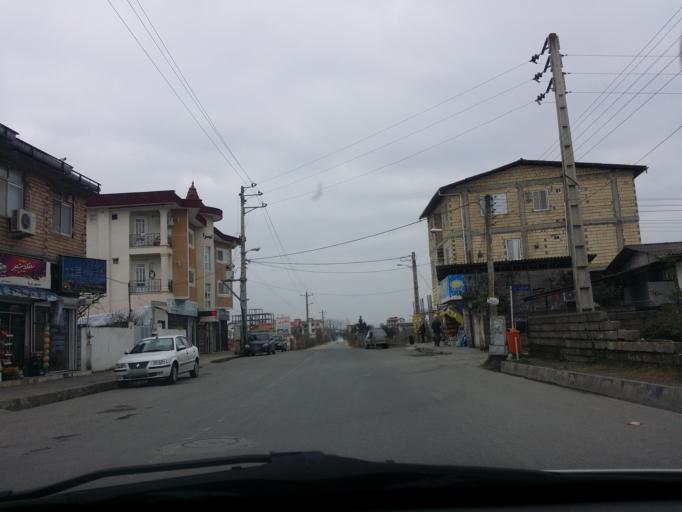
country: IR
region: Mazandaran
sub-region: Nowshahr
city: Nowshahr
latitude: 36.6431
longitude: 51.4848
